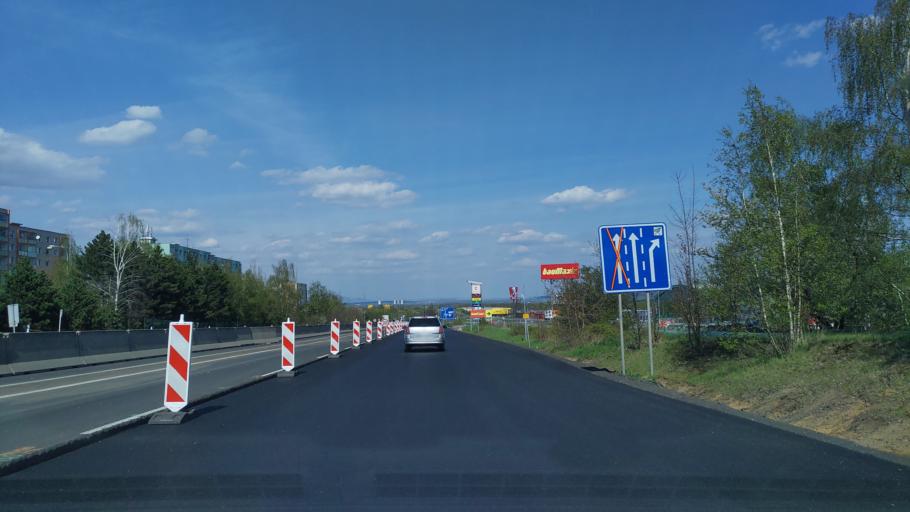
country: CZ
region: Ustecky
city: Jirkov
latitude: 50.4846
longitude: 13.4385
